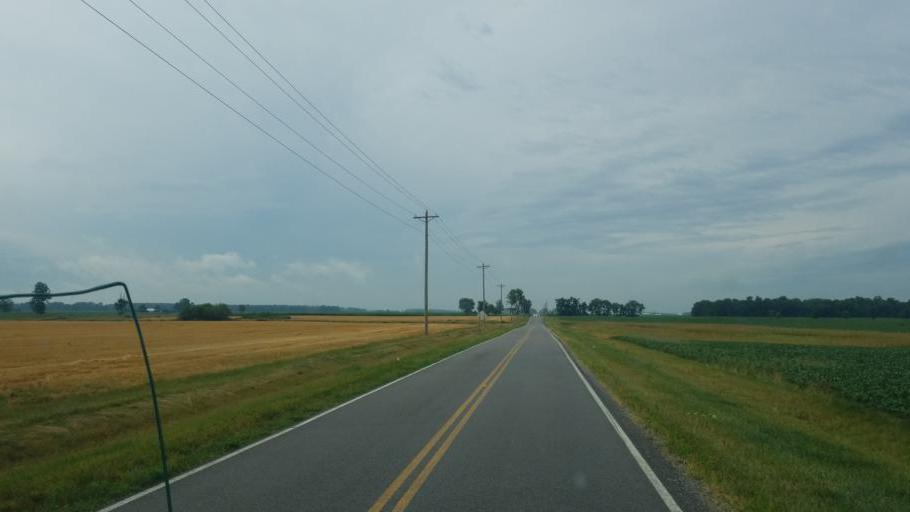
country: US
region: Ohio
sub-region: Defiance County
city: Hicksville
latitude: 41.3361
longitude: -84.6899
